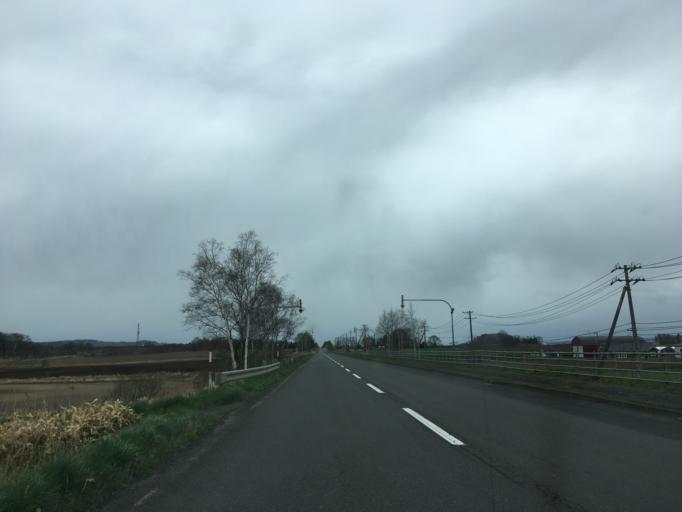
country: JP
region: Hokkaido
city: Chitose
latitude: 42.9077
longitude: 141.8118
